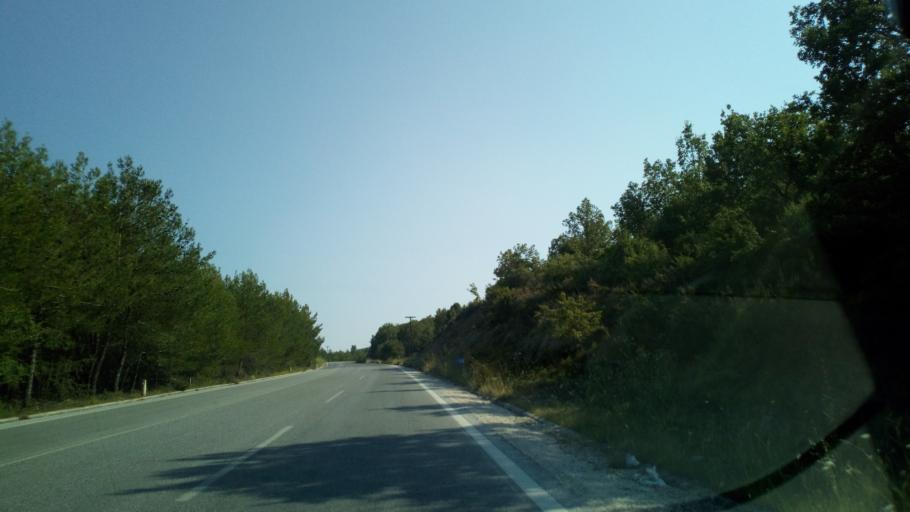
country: GR
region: Central Macedonia
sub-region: Nomos Chalkidikis
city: Polygyros
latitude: 40.4134
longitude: 23.4213
